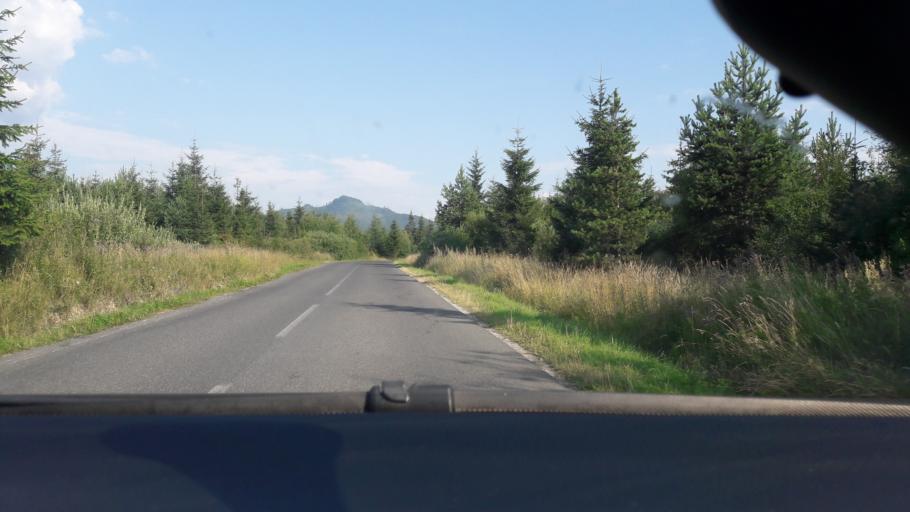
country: SK
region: Presovsky
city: Spisska Bela
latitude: 49.2028
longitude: 20.3747
